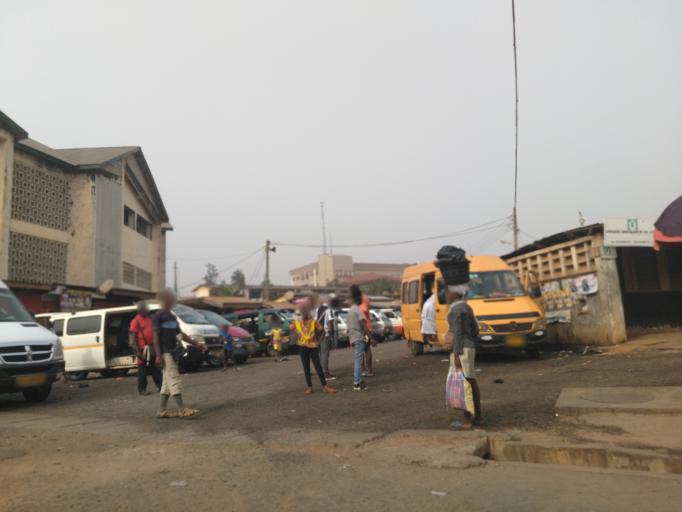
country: GH
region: Ashanti
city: Kumasi
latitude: 6.6926
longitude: -1.6231
